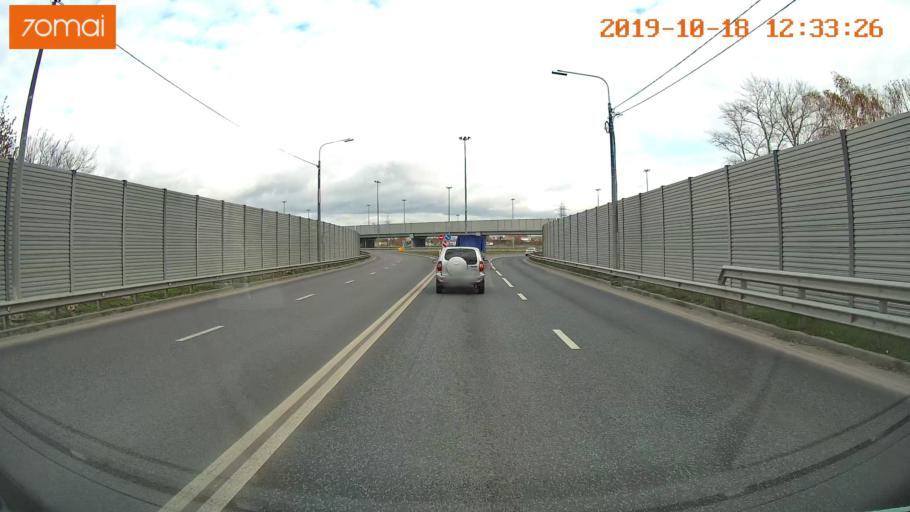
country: RU
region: Rjazan
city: Ryazan'
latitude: 54.6083
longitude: 39.6380
